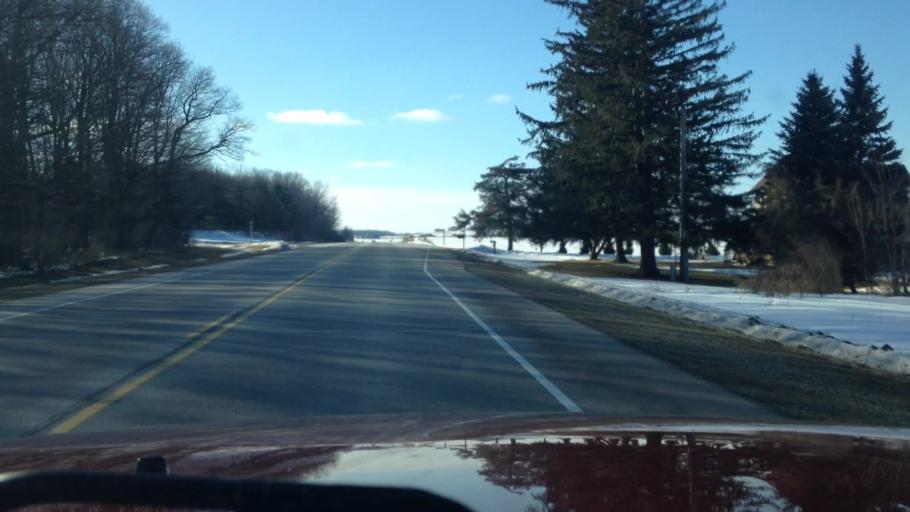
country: US
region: Wisconsin
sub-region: Waukesha County
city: Oconomowoc
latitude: 43.1870
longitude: -88.5084
